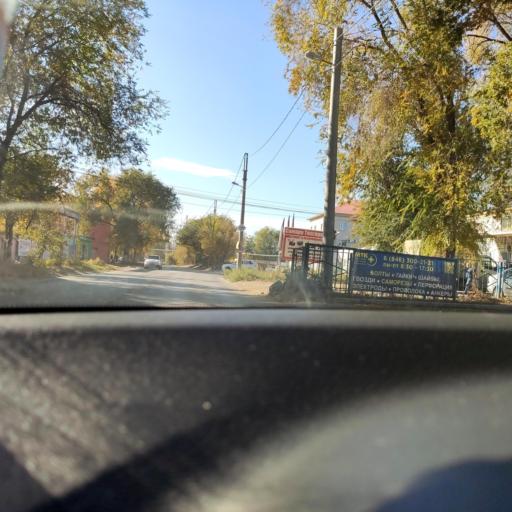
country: RU
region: Samara
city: Petra-Dubrava
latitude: 53.2443
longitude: 50.2997
